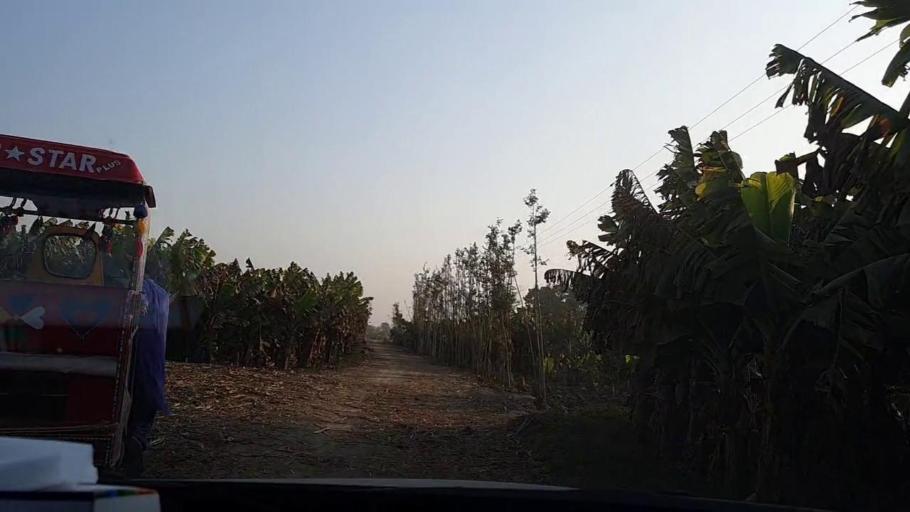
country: PK
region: Sindh
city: Tando Ghulam Ali
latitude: 25.2075
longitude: 68.9206
